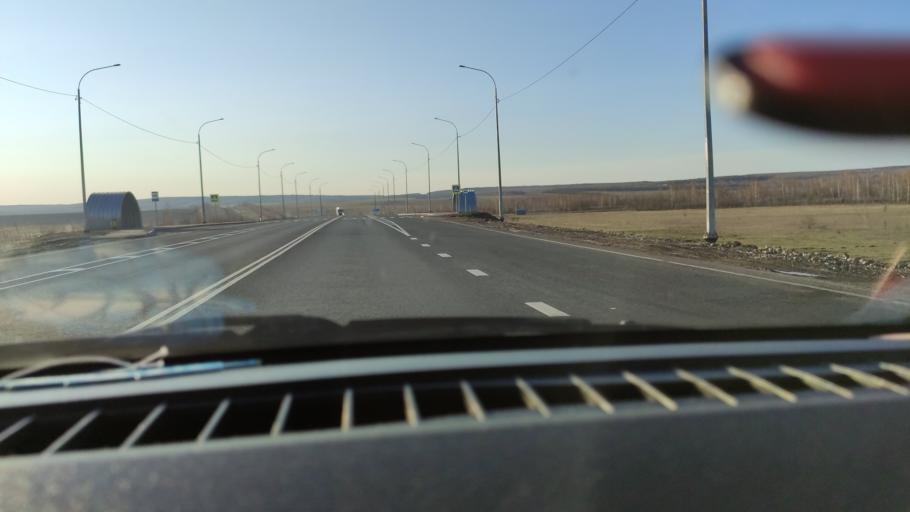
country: RU
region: Saratov
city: Shikhany
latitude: 52.1304
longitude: 47.2300
